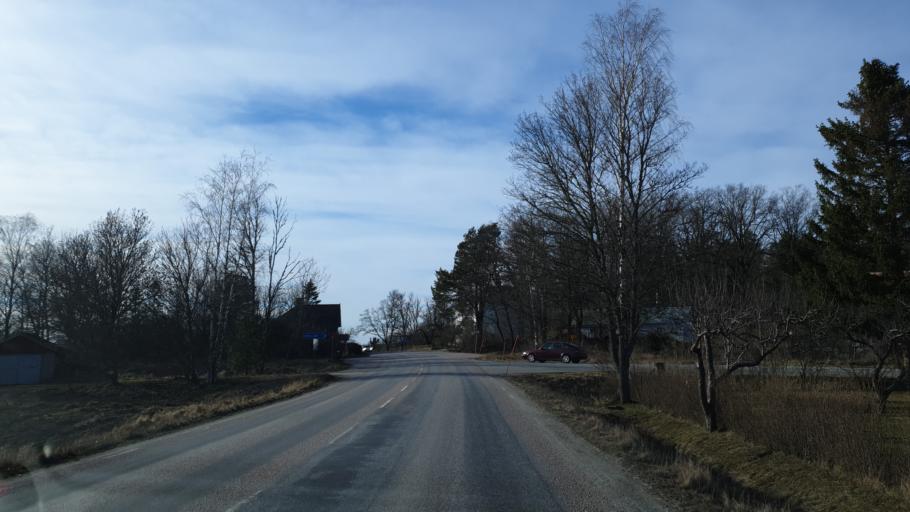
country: SE
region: Uppsala
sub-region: Enkopings Kommun
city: Grillby
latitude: 59.5920
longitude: 17.2009
